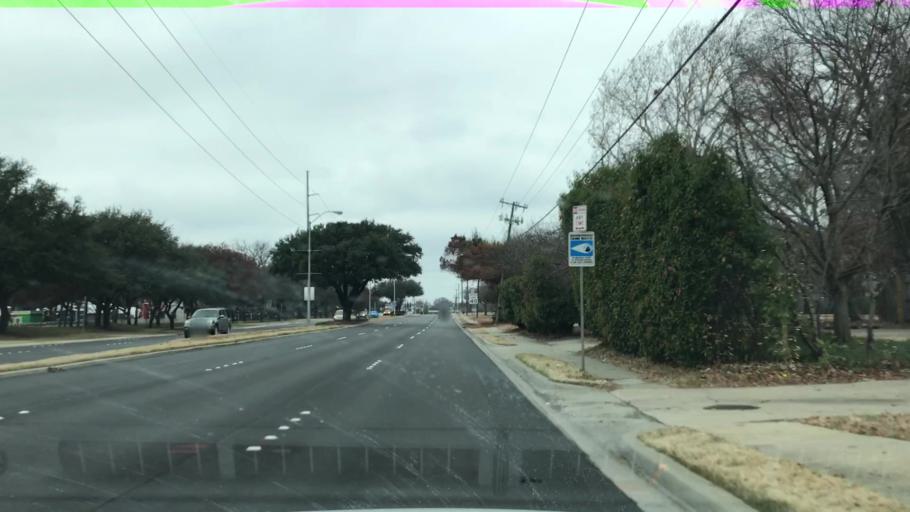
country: US
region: Texas
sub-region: Dallas County
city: Richardson
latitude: 32.9609
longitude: -96.7297
